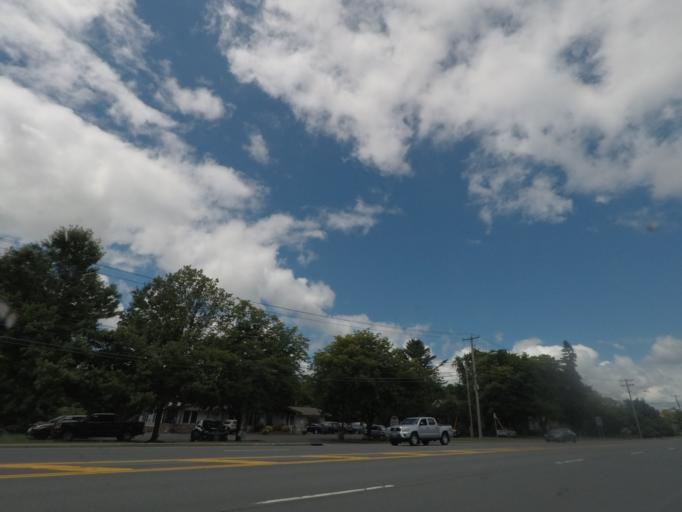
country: US
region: New York
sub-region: Albany County
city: Menands
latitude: 42.6572
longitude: -73.6931
